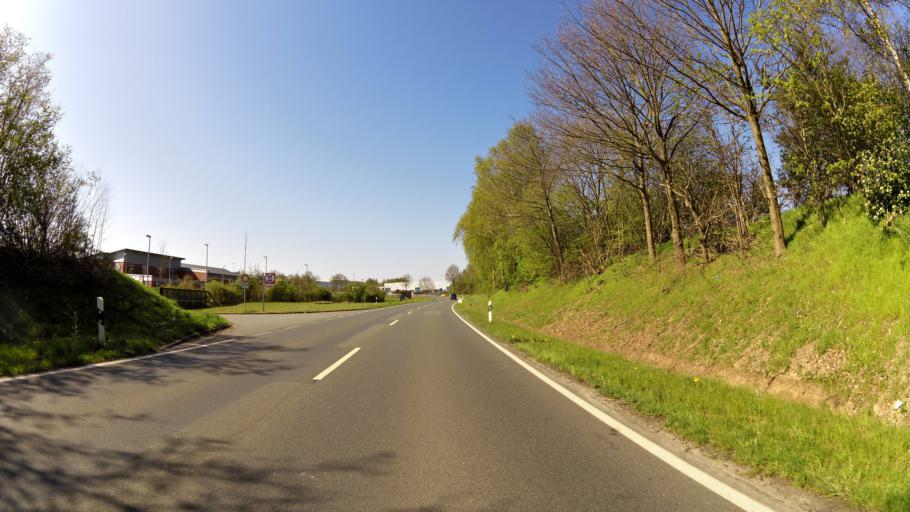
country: DE
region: Lower Saxony
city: Syke
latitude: 52.9210
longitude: 8.8028
